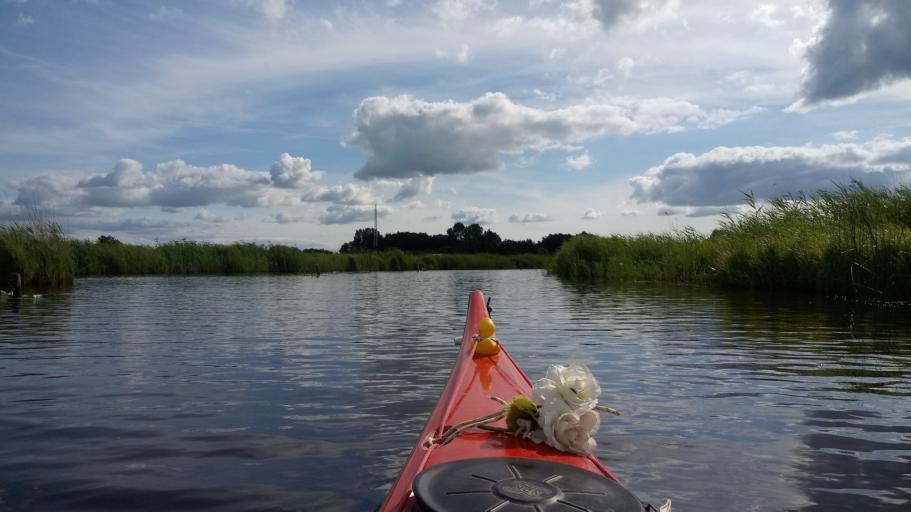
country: NL
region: Overijssel
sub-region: Gemeente Steenwijkerland
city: Wanneperveen
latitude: 52.7130
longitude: 6.1231
